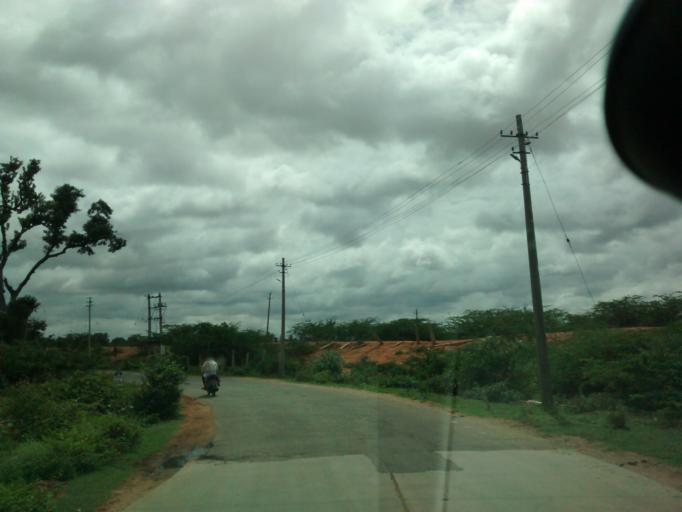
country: IN
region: Karnataka
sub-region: Tumkur
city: Kodigenahalli
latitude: 13.7066
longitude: 77.3745
